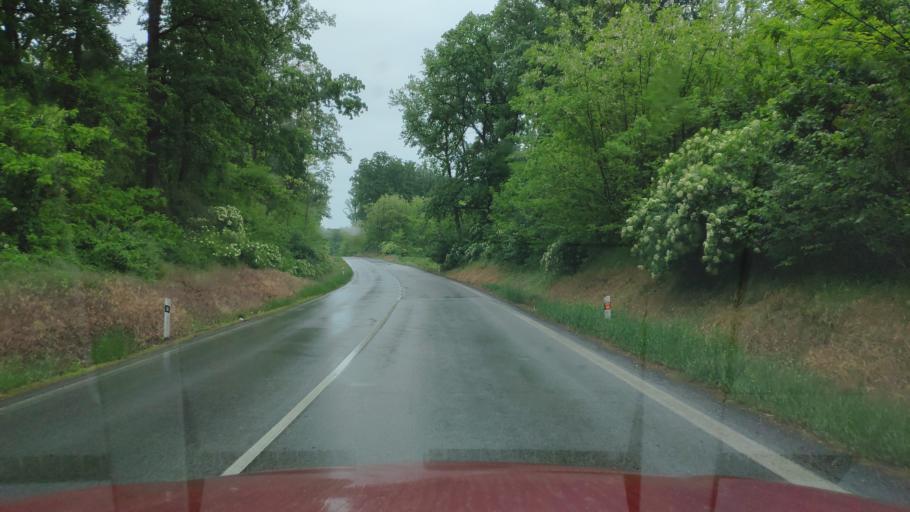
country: HU
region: Borsod-Abauj-Zemplen
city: Ricse
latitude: 48.4374
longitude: 21.9475
